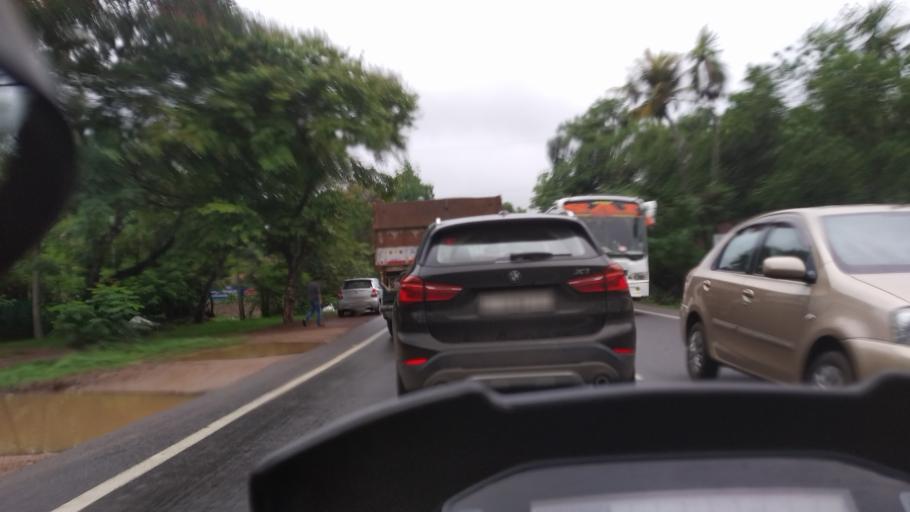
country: IN
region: Kerala
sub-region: Alappuzha
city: Mavelikara
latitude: 9.2954
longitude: 76.4342
